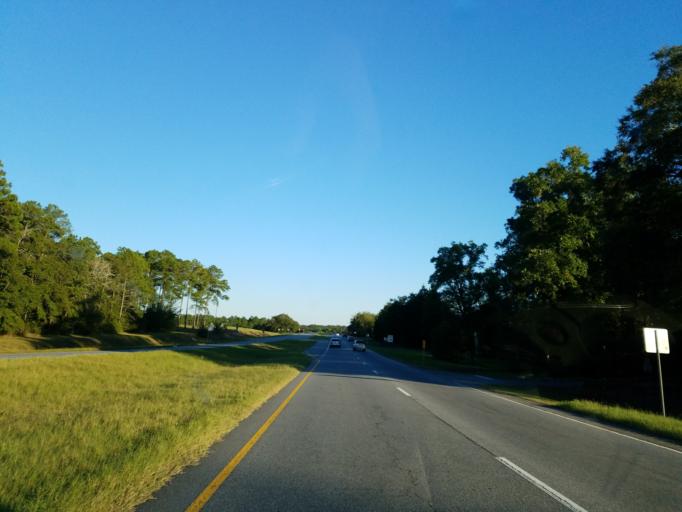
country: US
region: Georgia
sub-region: Worth County
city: Sylvester
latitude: 31.5162
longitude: -83.7824
